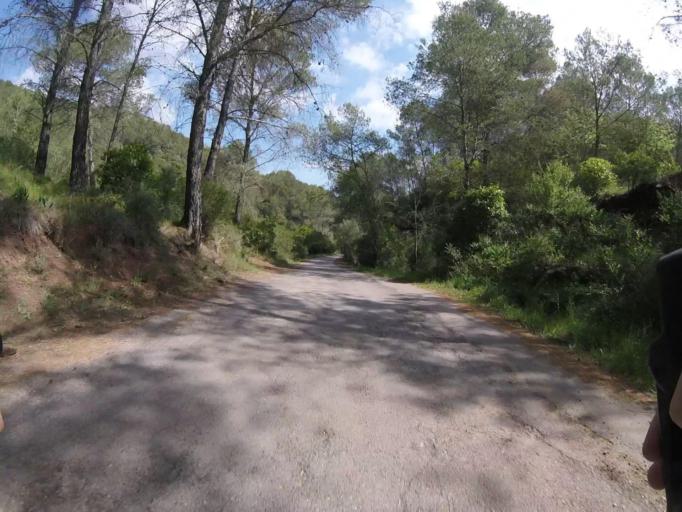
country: ES
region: Valencia
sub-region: Provincia de Castello
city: Cabanes
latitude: 40.1058
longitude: 0.0392
